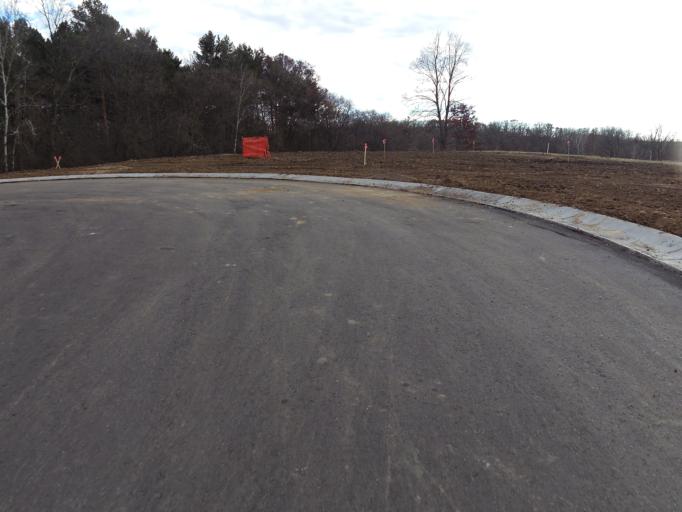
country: US
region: Minnesota
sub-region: Washington County
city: Lake Elmo
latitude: 44.9719
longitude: -92.8632
